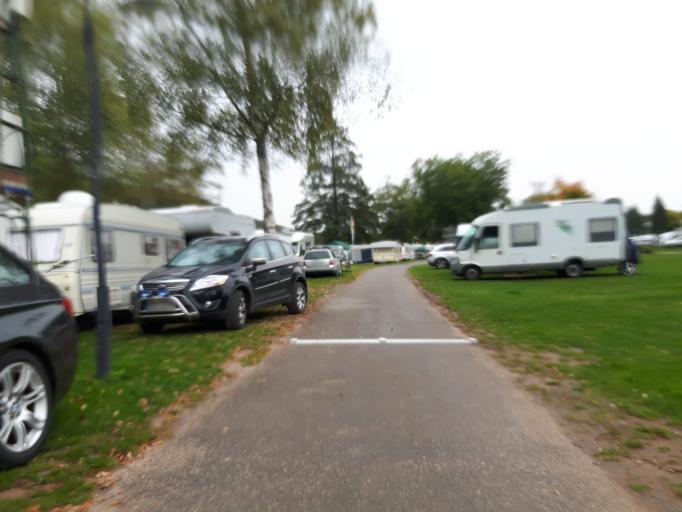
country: DE
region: Bavaria
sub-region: Regierungsbezirk Unterfranken
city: Kreuzwertheim
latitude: 49.7815
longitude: 9.5654
